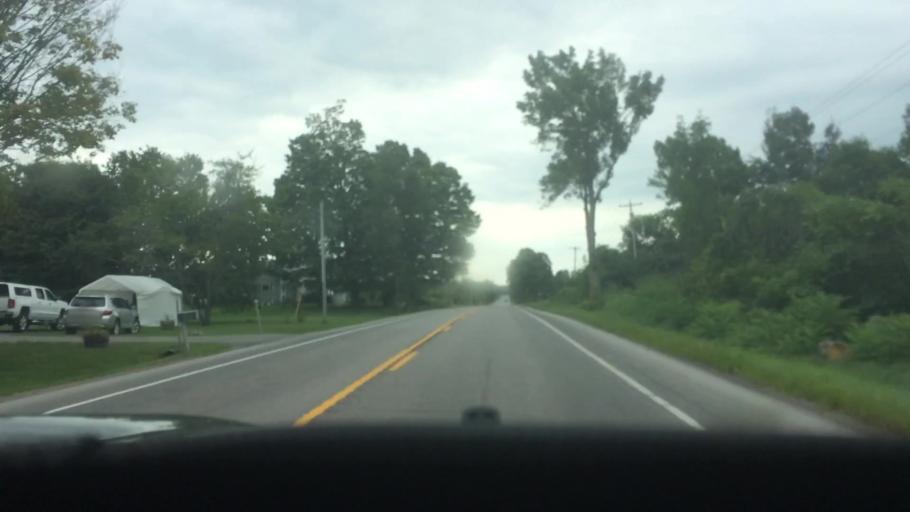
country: US
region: New York
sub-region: St. Lawrence County
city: Ogdensburg
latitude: 44.6083
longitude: -75.3955
